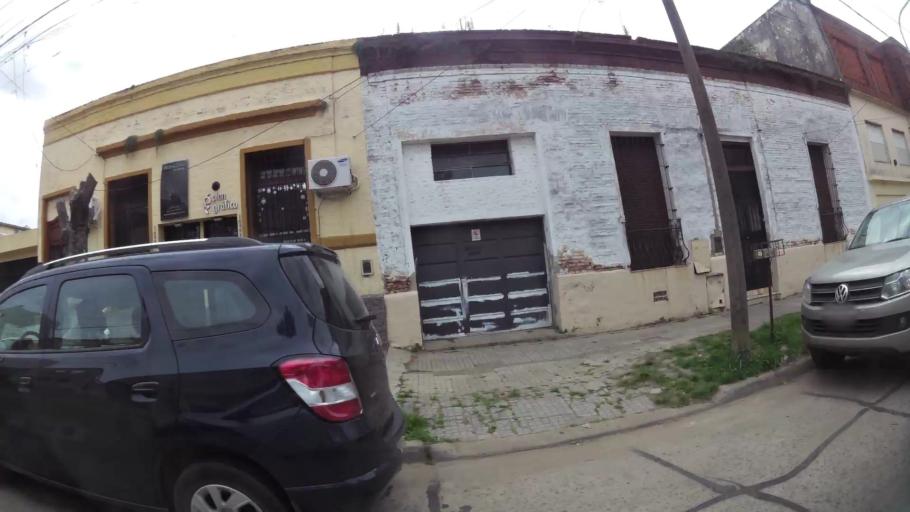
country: AR
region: Buenos Aires
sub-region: Partido de Campana
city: Campana
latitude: -34.1634
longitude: -58.9638
